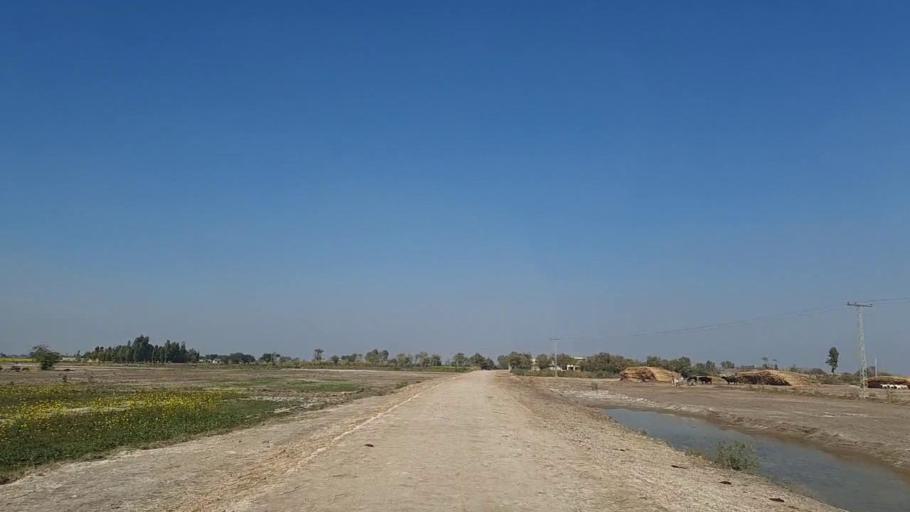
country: PK
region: Sindh
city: Bandhi
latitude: 26.5448
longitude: 68.3270
